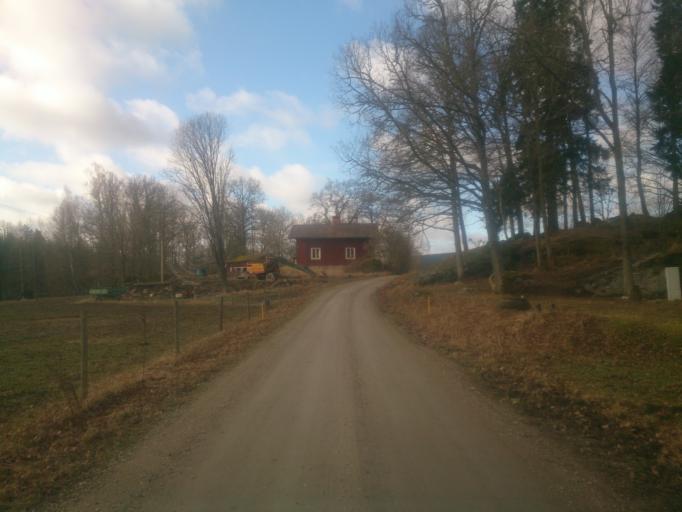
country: SE
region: OEstergoetland
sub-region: Atvidabergs Kommun
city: Atvidaberg
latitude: 58.1935
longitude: 16.1526
